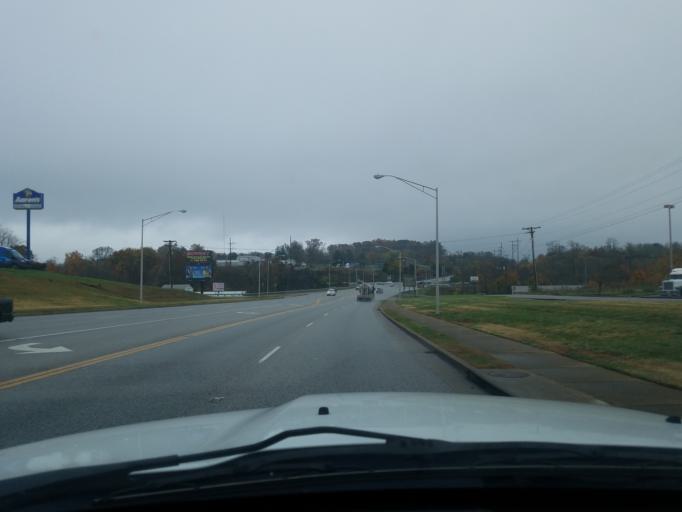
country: US
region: Kentucky
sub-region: Taylor County
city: Campbellsville
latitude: 37.3405
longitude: -85.3618
